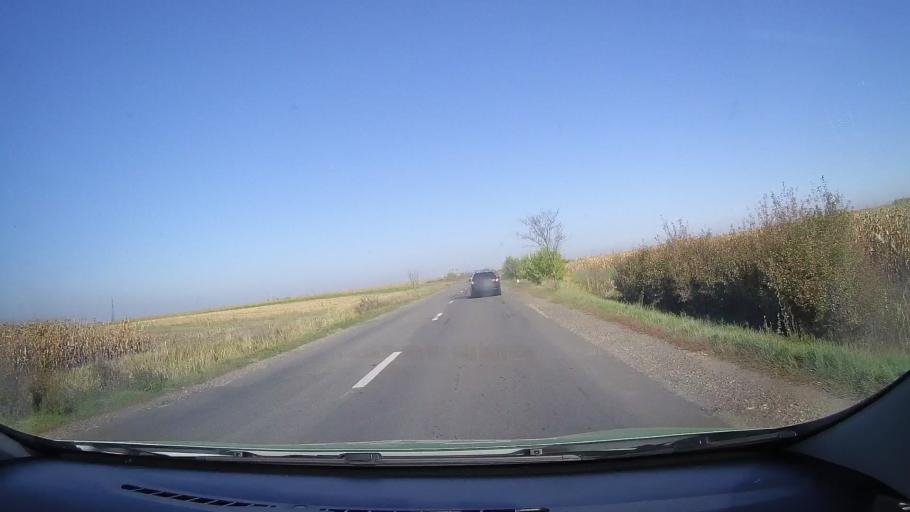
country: RO
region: Satu Mare
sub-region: Comuna Cauas
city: Cauas
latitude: 47.6137
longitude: 22.5376
